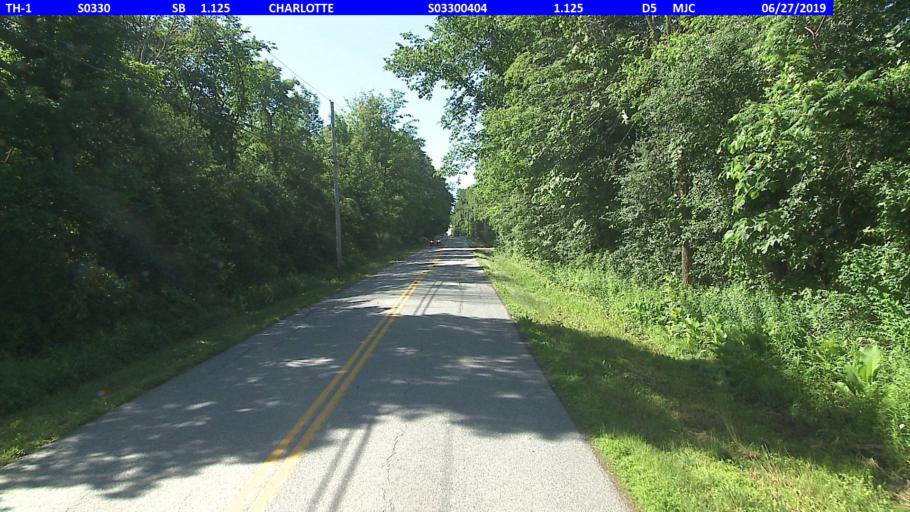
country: US
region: Vermont
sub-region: Chittenden County
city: Hinesburg
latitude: 44.3355
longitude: -73.1928
